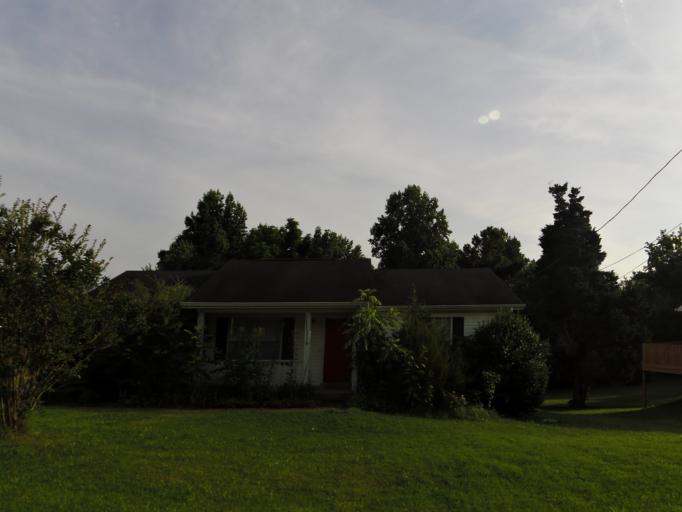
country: US
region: Tennessee
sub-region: Dickson County
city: Burns
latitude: 36.0573
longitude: -87.3333
